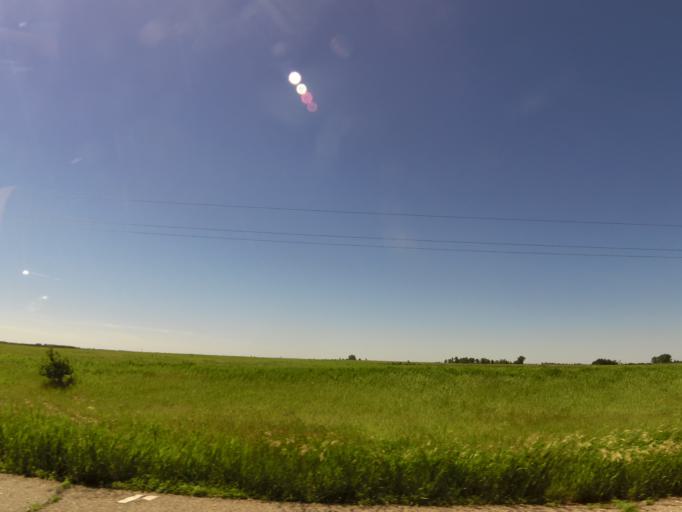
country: US
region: Minnesota
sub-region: Red Lake County
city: Red Lake Falls
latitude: 47.7602
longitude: -96.3326
